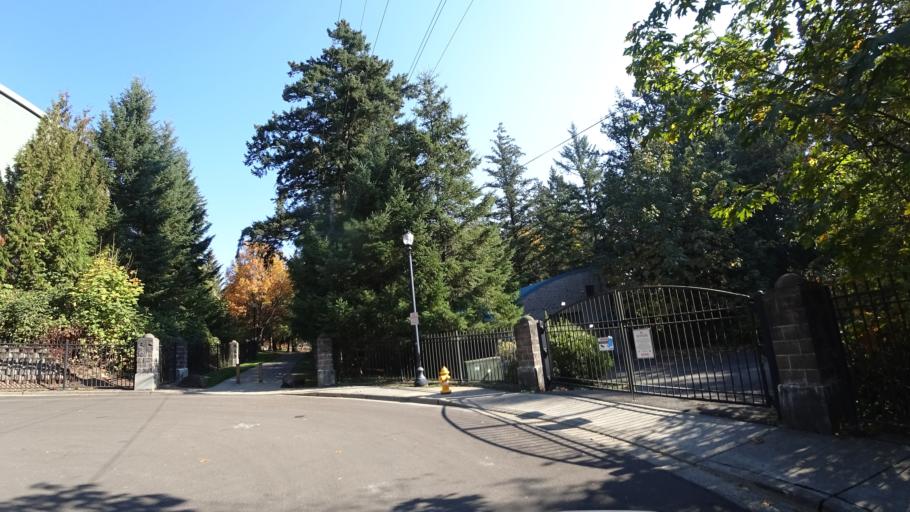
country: US
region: Oregon
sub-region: Multnomah County
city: Gresham
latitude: 45.4985
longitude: -122.4533
